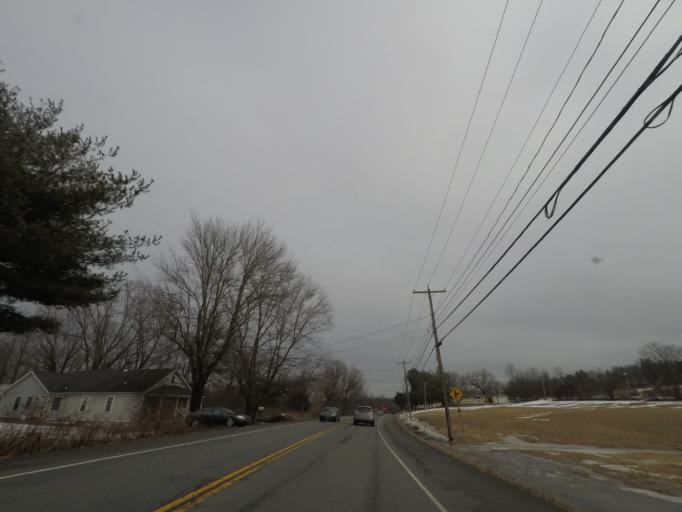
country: US
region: New York
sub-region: Albany County
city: Voorheesville
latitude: 42.7032
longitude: -73.9508
